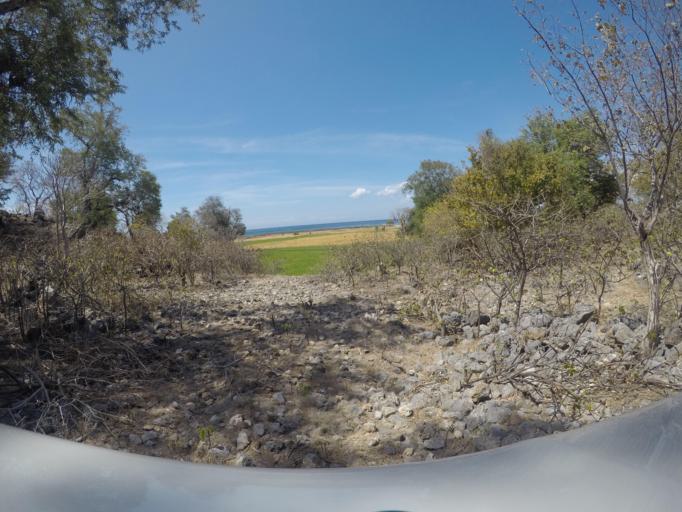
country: TL
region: Baucau
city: Baucau
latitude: -8.4304
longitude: 126.4423
